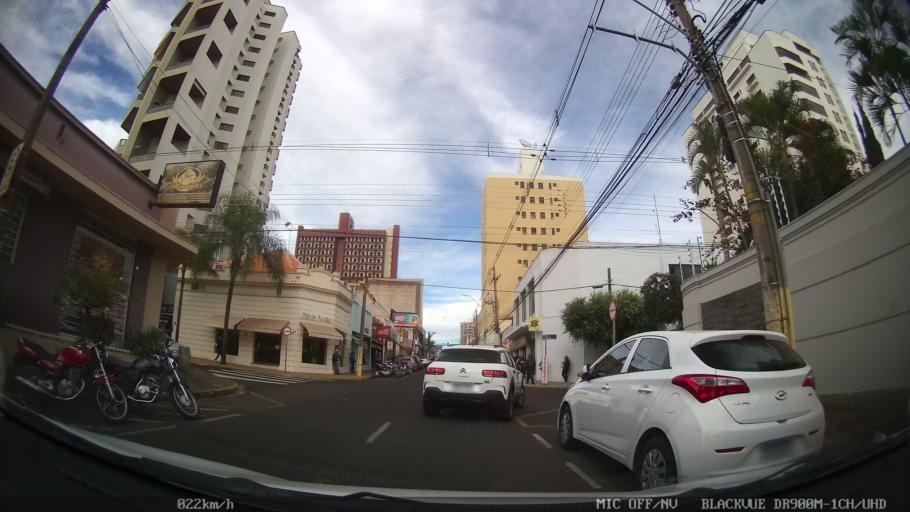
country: BR
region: Sao Paulo
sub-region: Catanduva
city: Catanduva
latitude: -21.1365
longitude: -48.9736
